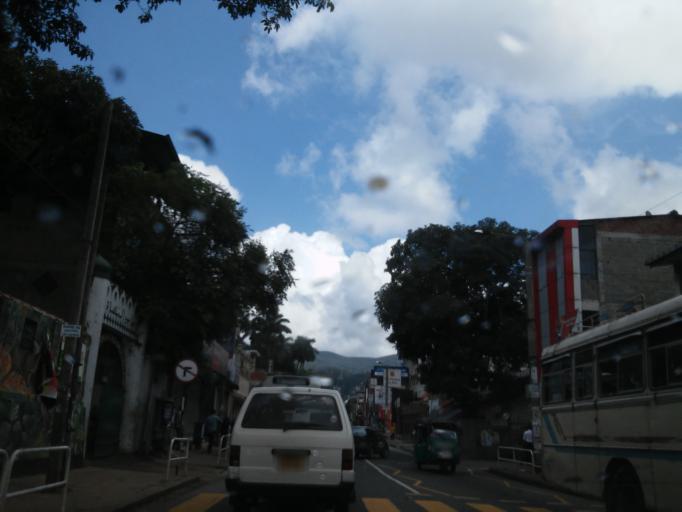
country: LK
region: Central
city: Kandy
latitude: 7.3013
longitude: 80.6361
